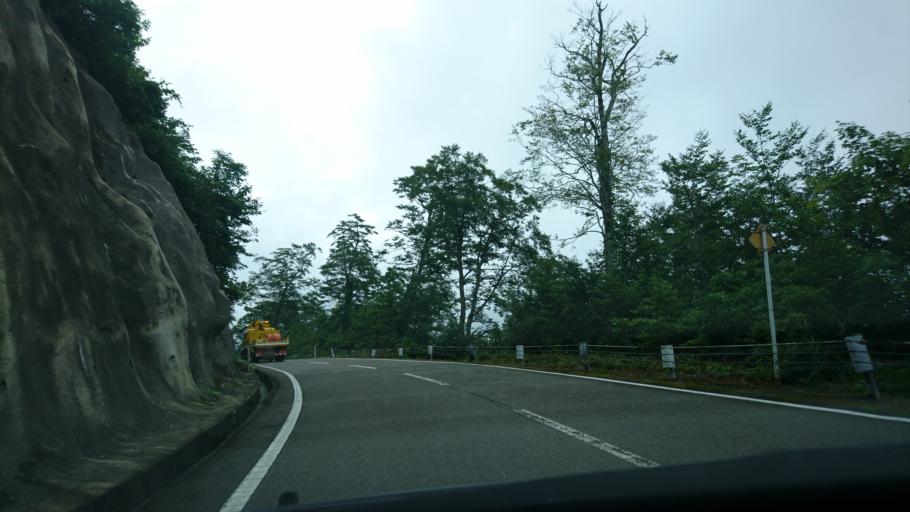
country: JP
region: Akita
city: Yuzawa
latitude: 38.9839
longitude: 140.7347
